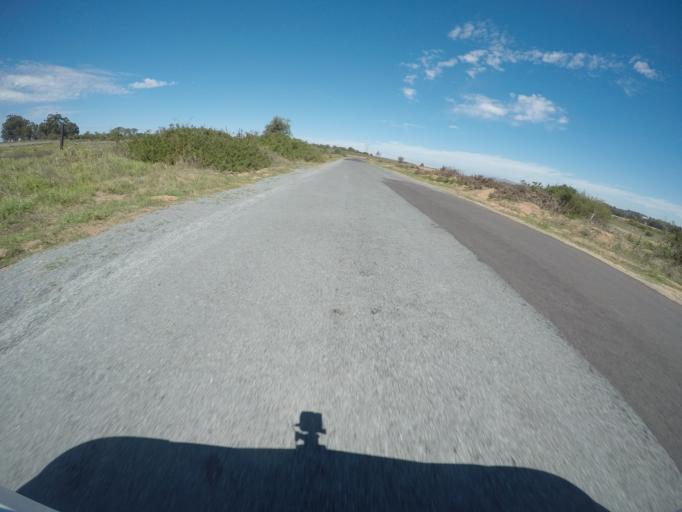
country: ZA
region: Western Cape
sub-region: West Coast District Municipality
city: Malmesbury
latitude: -33.5872
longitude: 18.6467
